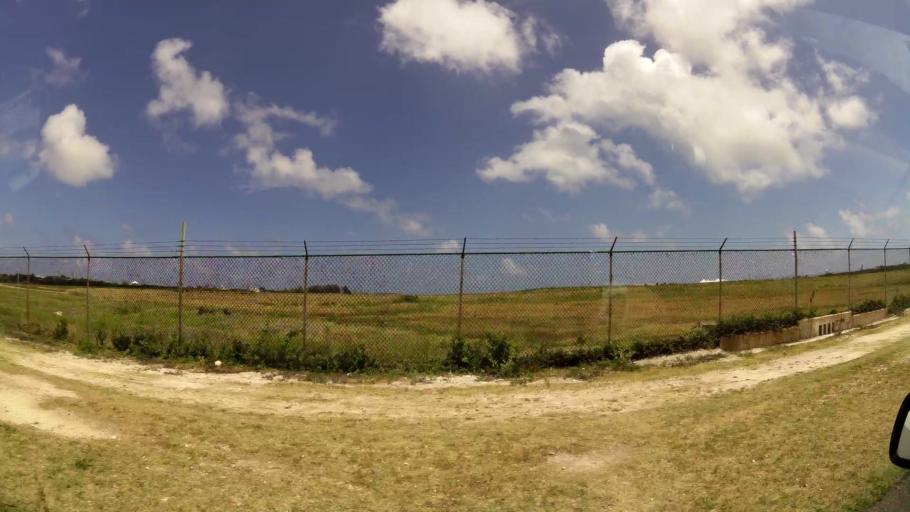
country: TC
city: Cockburn Town
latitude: 21.4465
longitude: -71.1528
